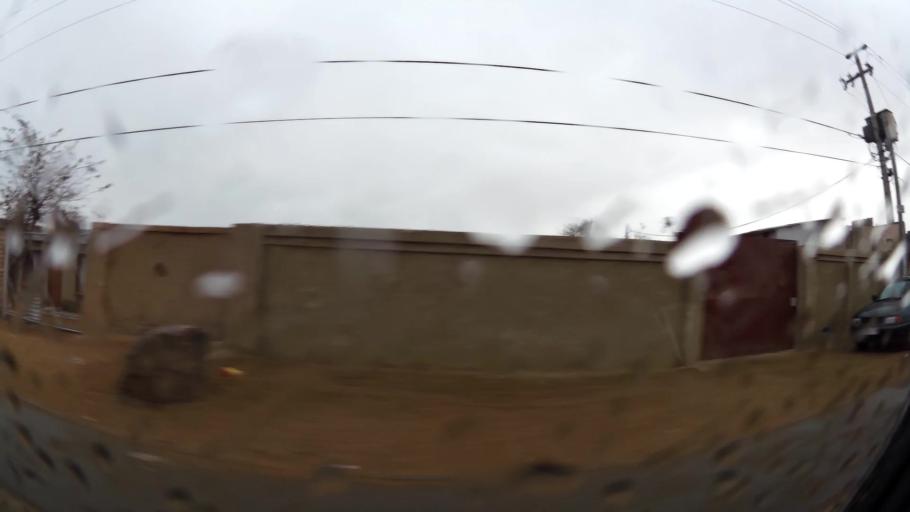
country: ZA
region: Gauteng
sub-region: City of Johannesburg Metropolitan Municipality
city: Roodepoort
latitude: -26.1761
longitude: 27.7910
